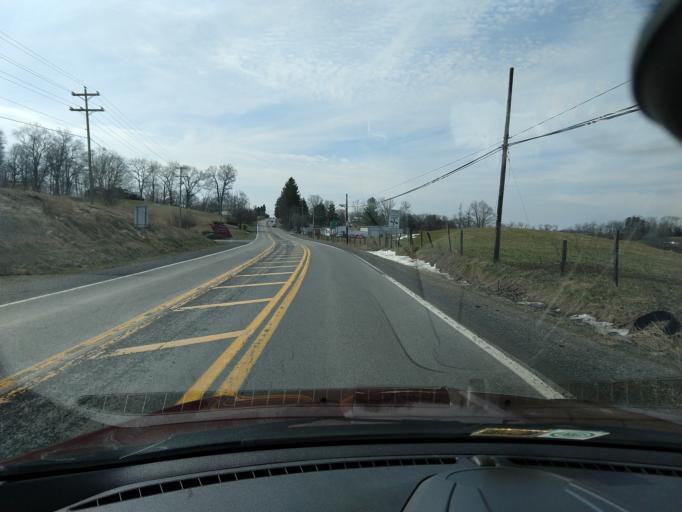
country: US
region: West Virginia
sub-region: Greenbrier County
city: Lewisburg
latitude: 37.8582
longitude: -80.4118
